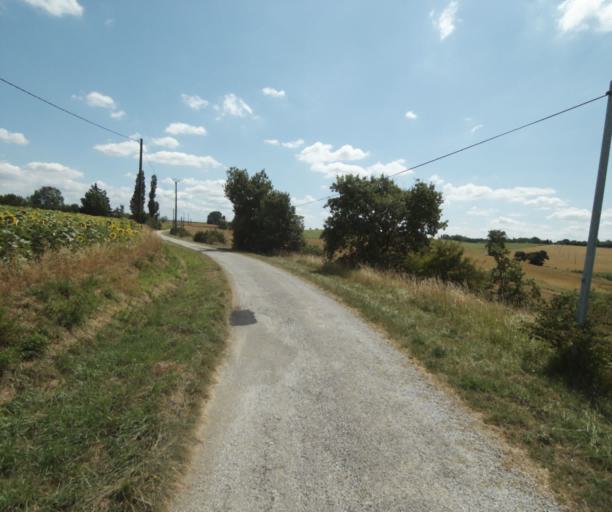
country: FR
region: Midi-Pyrenees
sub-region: Departement de la Haute-Garonne
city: Auriac-sur-Vendinelle
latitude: 43.4683
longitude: 1.8293
